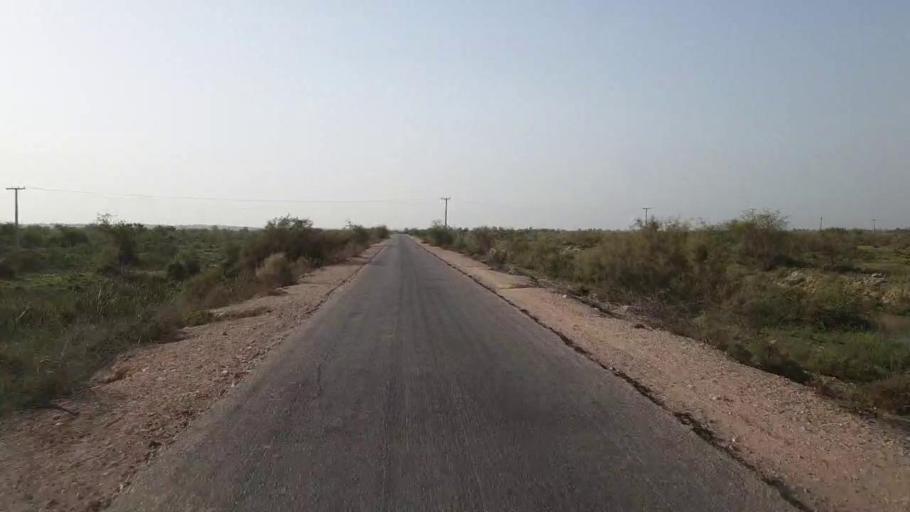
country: PK
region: Sindh
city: Jam Sahib
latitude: 26.4510
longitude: 68.8625
